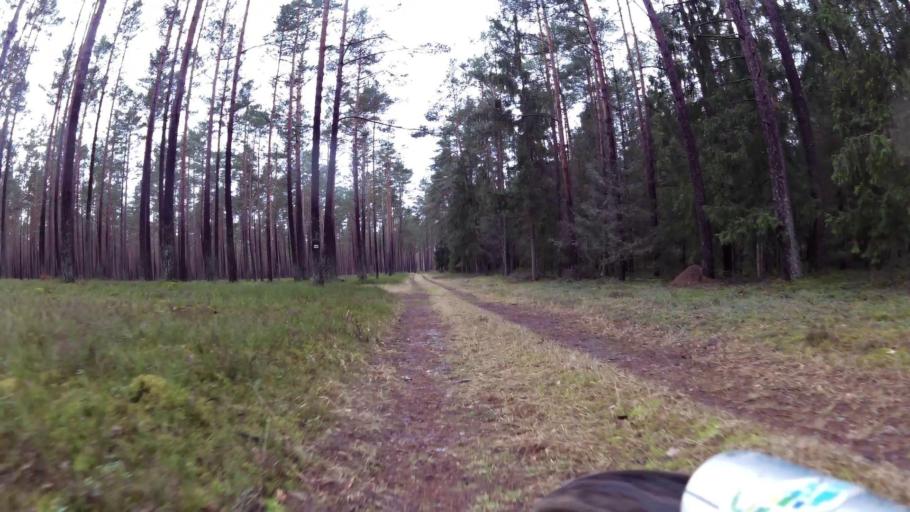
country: PL
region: Pomeranian Voivodeship
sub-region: Powiat bytowski
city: Kolczyglowy
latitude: 54.2392
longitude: 17.2673
